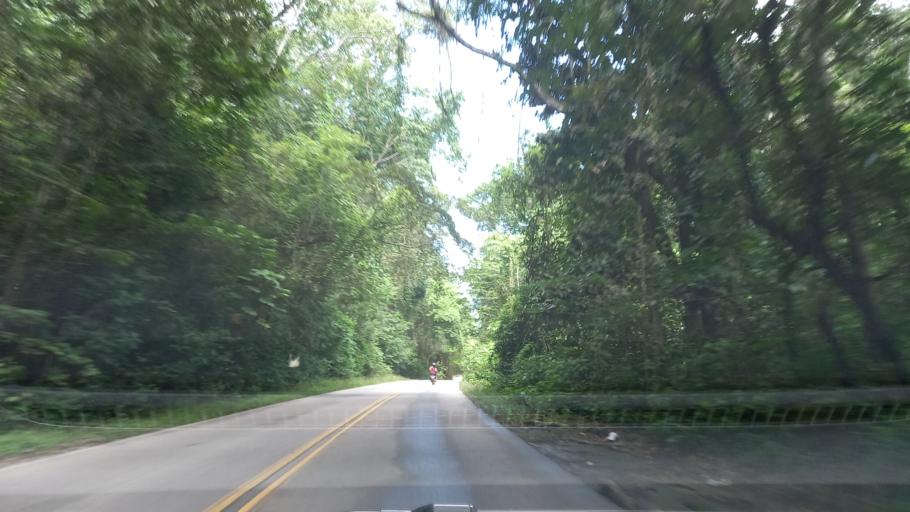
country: BR
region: Pernambuco
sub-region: Rio Formoso
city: Rio Formoso
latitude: -8.7364
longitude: -35.1724
